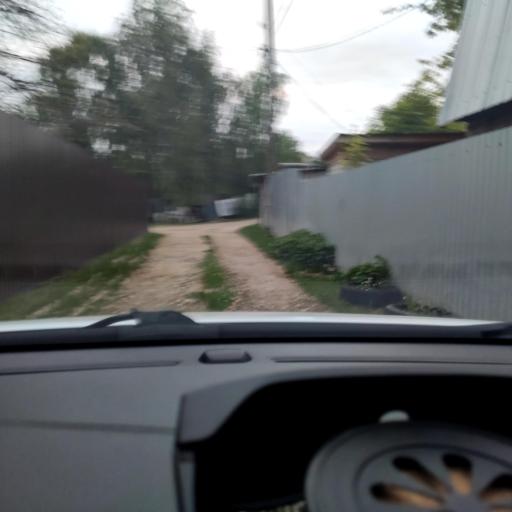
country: RU
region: Tatarstan
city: Vysokaya Gora
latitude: 55.8534
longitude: 49.2499
